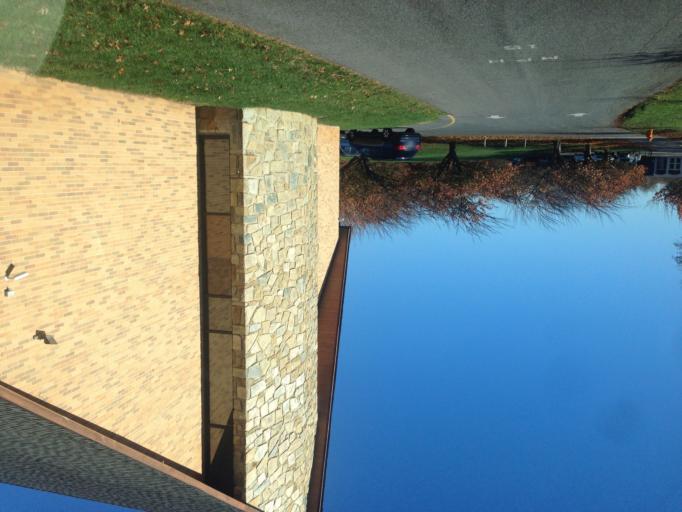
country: US
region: Maryland
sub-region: Howard County
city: Riverside
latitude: 39.1923
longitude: -76.8686
